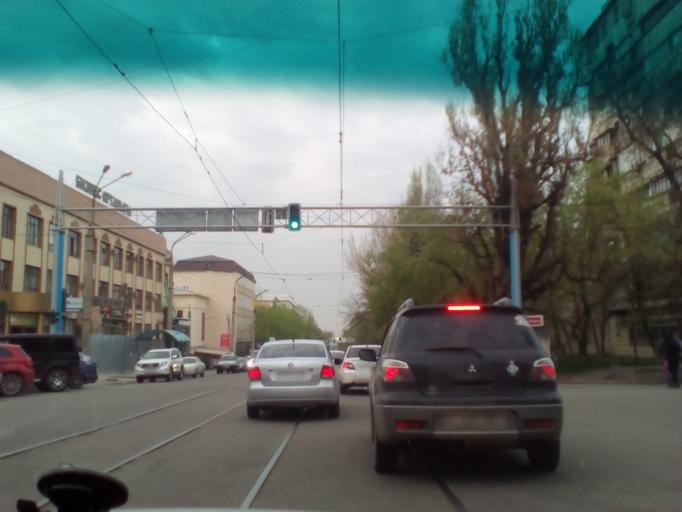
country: KZ
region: Almaty Qalasy
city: Almaty
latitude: 43.2618
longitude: 76.9492
